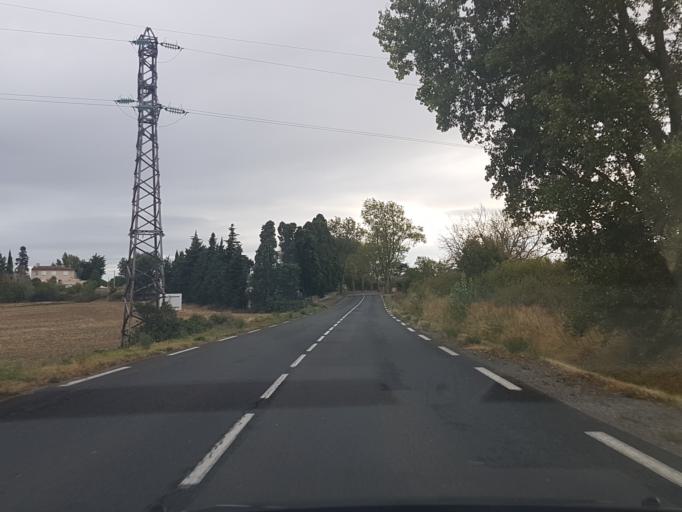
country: FR
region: Languedoc-Roussillon
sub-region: Departement de l'Aude
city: Bram
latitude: 43.2331
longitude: 2.0986
